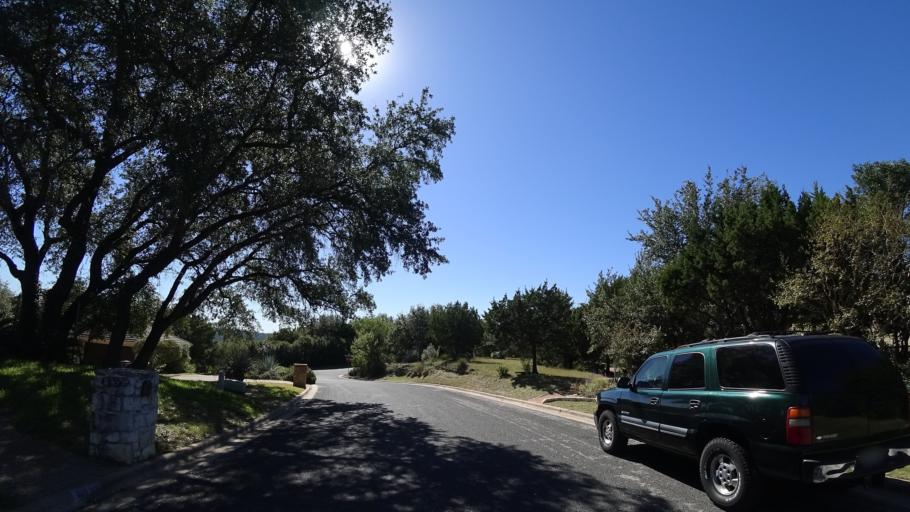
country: US
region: Texas
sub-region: Travis County
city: West Lake Hills
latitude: 30.3478
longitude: -97.7821
